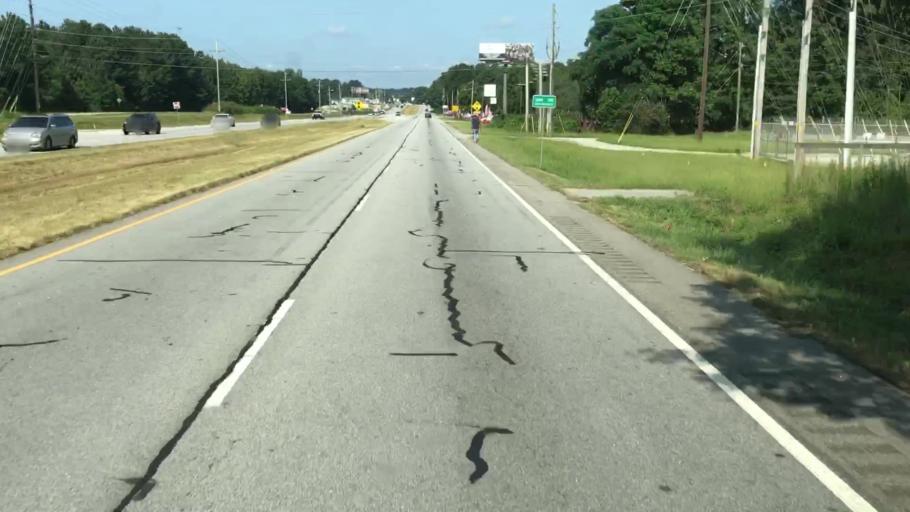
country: US
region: Georgia
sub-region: Walton County
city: Loganville
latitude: 33.8295
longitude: -83.8408
